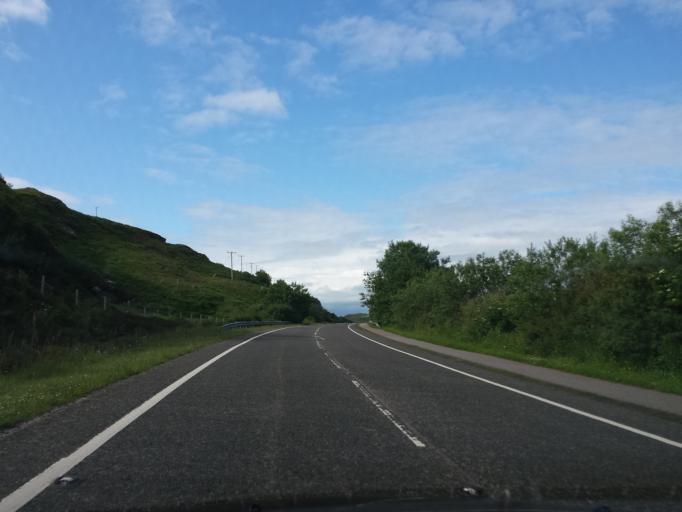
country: GB
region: Scotland
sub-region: Argyll and Bute
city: Isle Of Mull
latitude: 56.9787
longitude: -5.8287
